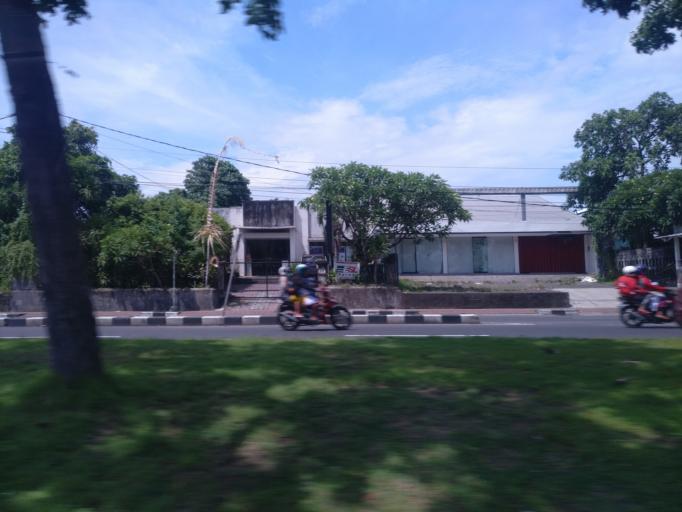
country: ID
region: Bali
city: Banjar Kertajiwa
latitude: -8.6491
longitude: 115.2644
